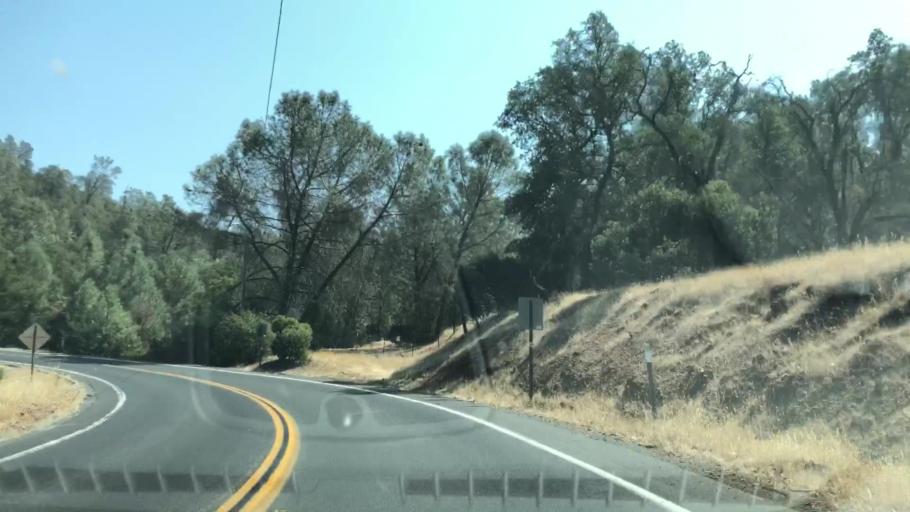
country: US
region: California
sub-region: Calaveras County
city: Copperopolis
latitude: 37.8951
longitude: -120.5651
